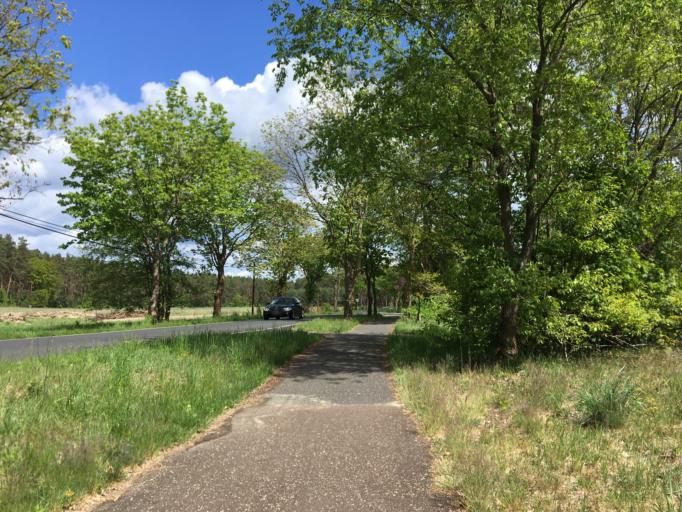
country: DE
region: Brandenburg
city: Liebenwalde
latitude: 52.8920
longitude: 13.4961
